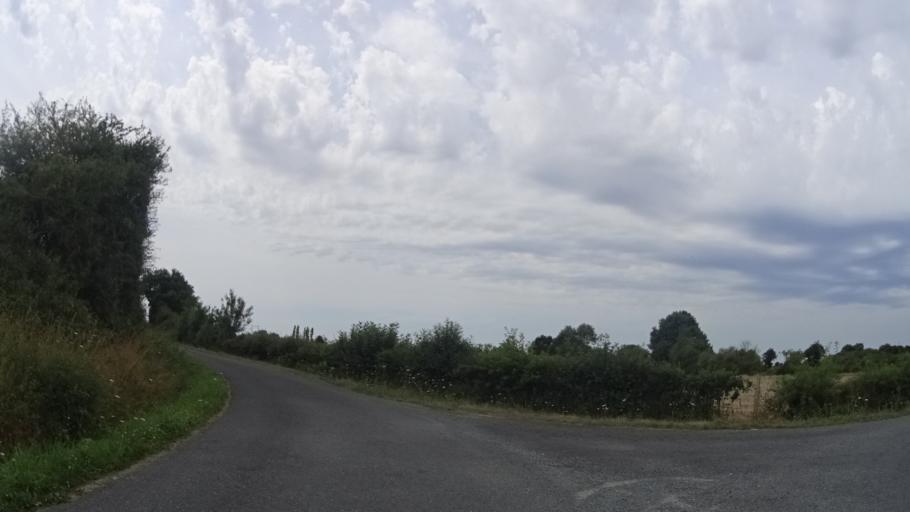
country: FR
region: Pays de la Loire
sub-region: Departement de la Loire-Atlantique
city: Blain
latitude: 47.4428
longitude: -1.7214
